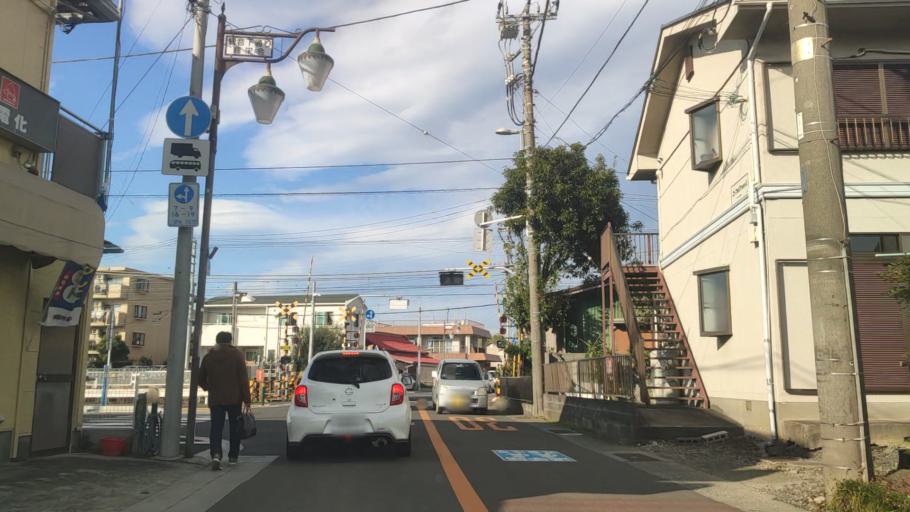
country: JP
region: Kanagawa
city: Zama
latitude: 35.4574
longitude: 139.3987
